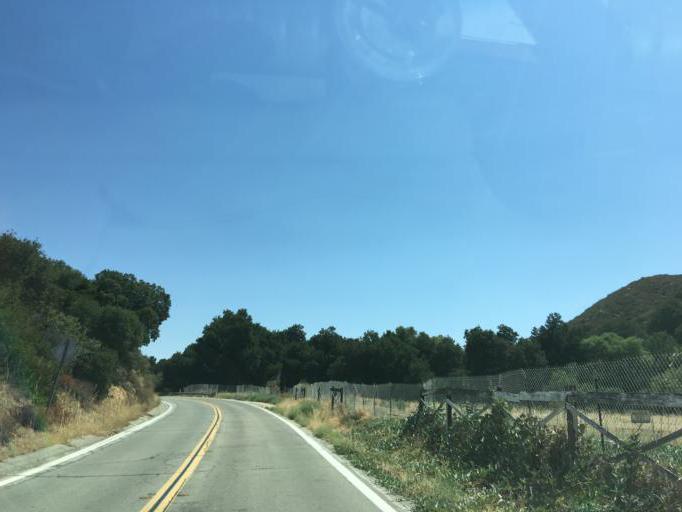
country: US
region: California
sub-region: Los Angeles County
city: Green Valley
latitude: 34.6147
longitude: -118.4263
